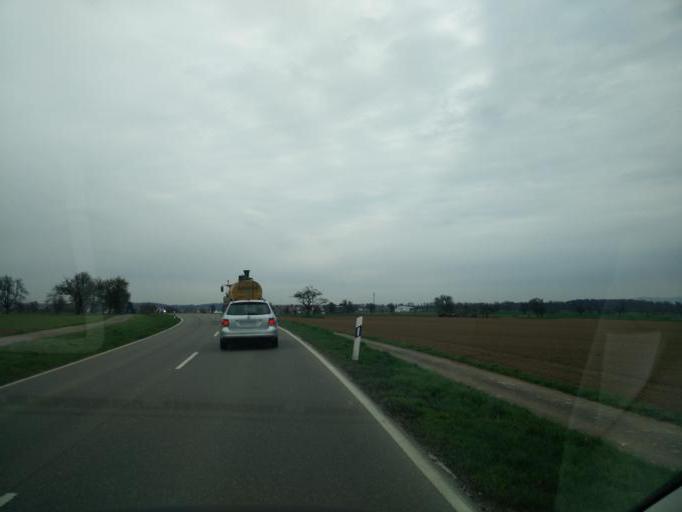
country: DE
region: Baden-Wuerttemberg
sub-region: Tuebingen Region
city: Kusterdingen
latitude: 48.5117
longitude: 9.1136
